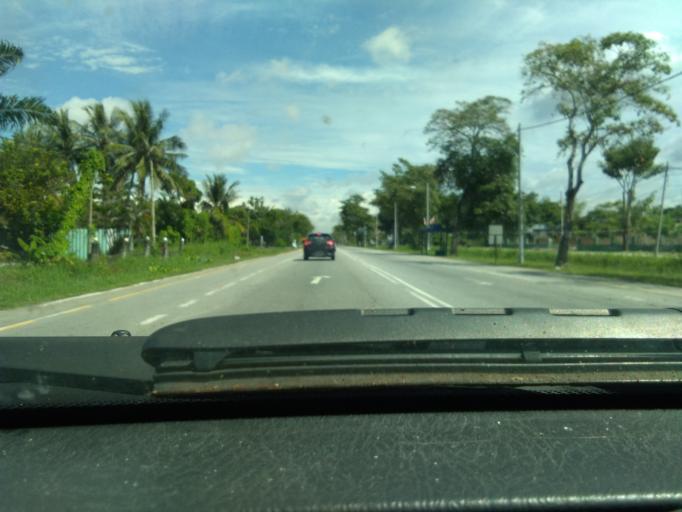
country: MY
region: Perak
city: Parit Buntar
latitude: 5.1053
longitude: 100.4852
